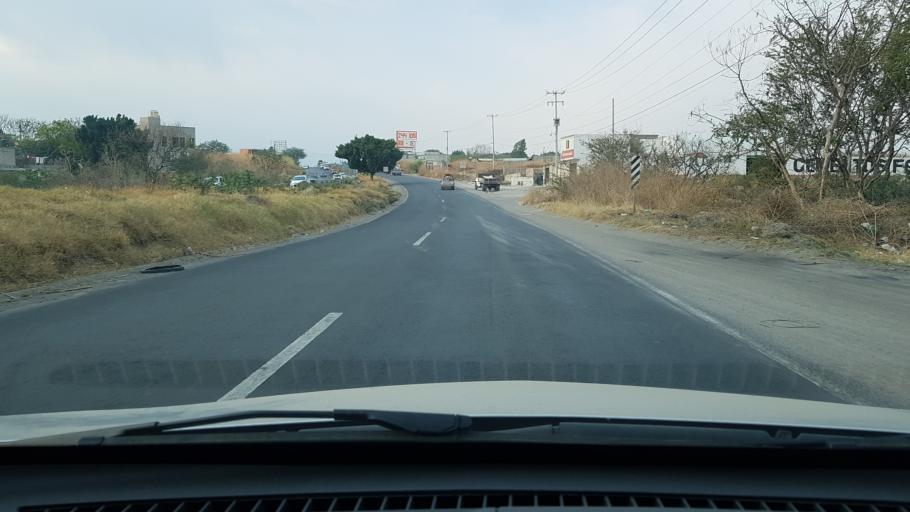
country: MX
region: Morelos
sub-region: Yecapixtla
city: Juan Morales
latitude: 18.8069
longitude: -98.9153
